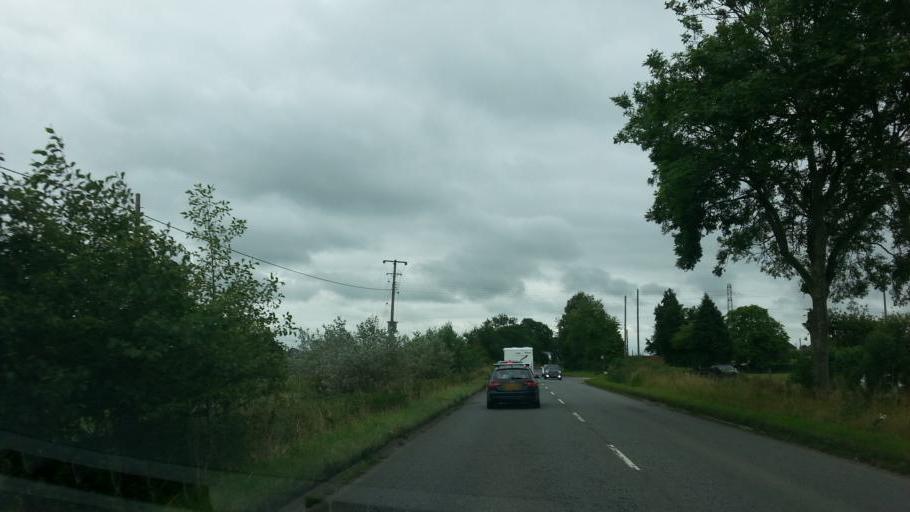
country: GB
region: England
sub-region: Wiltshire
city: Lacock
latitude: 51.4020
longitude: -2.1250
